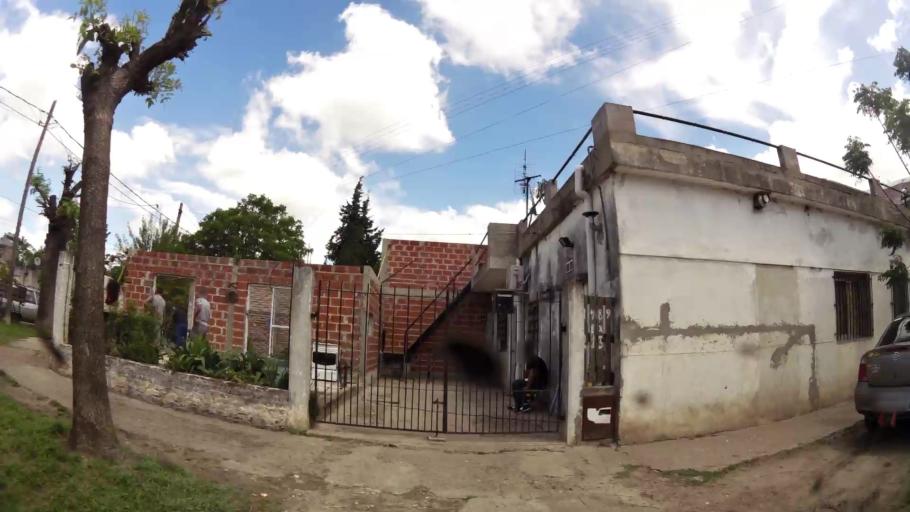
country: AR
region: Buenos Aires
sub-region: Partido de Quilmes
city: Quilmes
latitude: -34.8233
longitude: -58.2293
